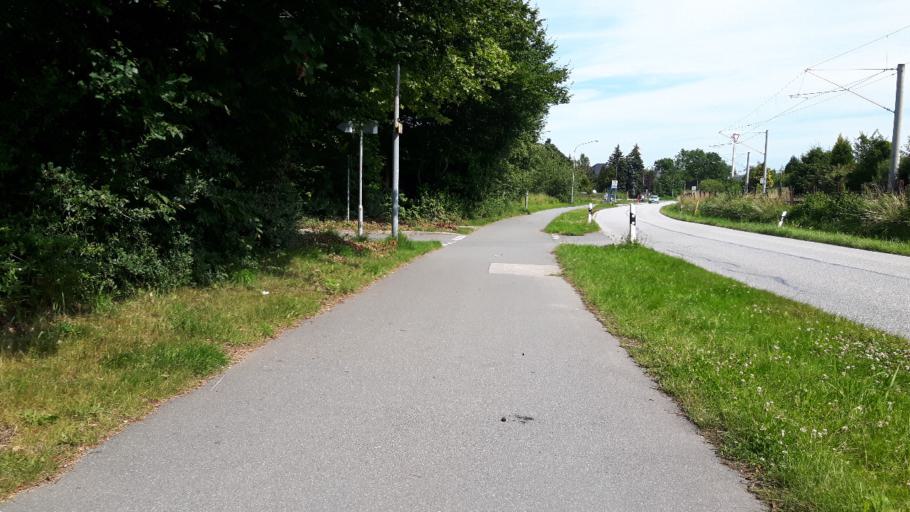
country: DE
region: Schleswig-Holstein
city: Travemuende
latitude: 53.9537
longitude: 10.8531
